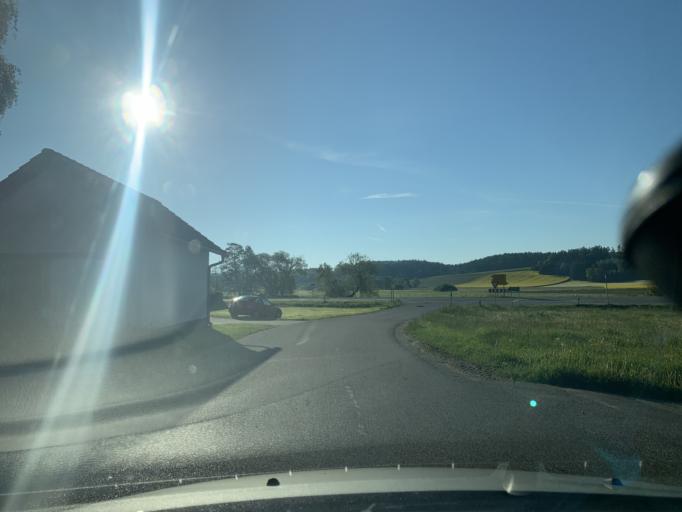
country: DE
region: Bavaria
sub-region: Lower Bavaria
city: Schalkham
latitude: 48.4790
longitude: 12.3886
